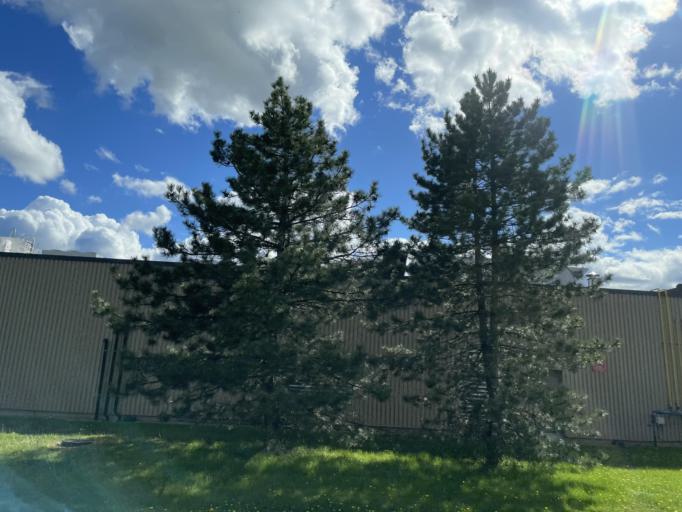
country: CA
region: Ontario
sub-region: Wellington County
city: Guelph
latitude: 43.4913
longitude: -80.2074
